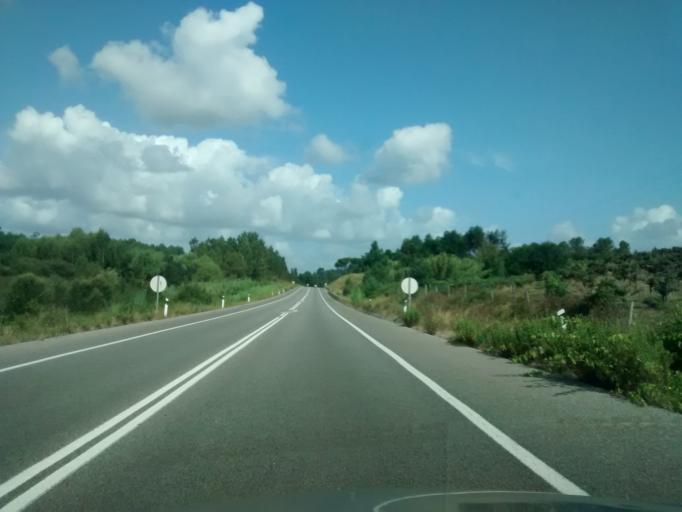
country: PT
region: Aveiro
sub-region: Anadia
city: Sangalhos
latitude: 40.4973
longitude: -8.4834
